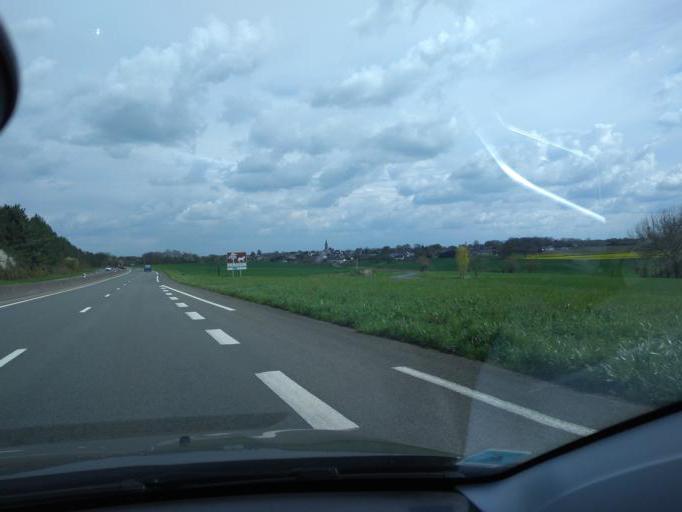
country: FR
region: Pays de la Loire
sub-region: Departement de Maine-et-Loire
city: Segre
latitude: 47.6693
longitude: -0.7854
